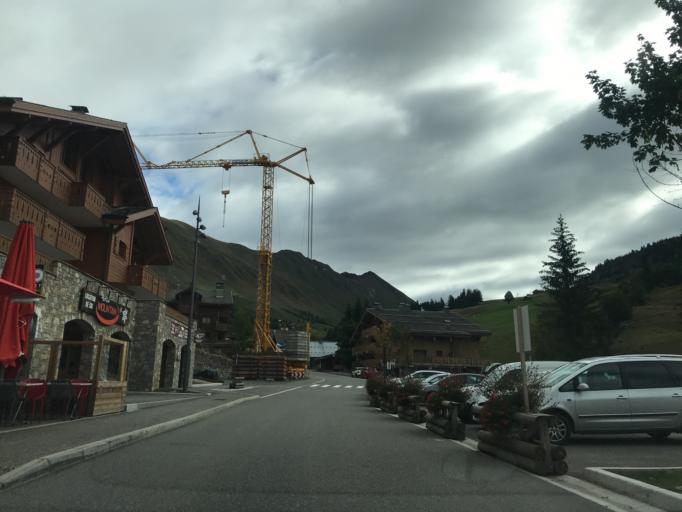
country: FR
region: Rhone-Alpes
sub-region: Departement de la Haute-Savoie
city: Le Grand-Bornand
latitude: 45.9737
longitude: 6.4542
